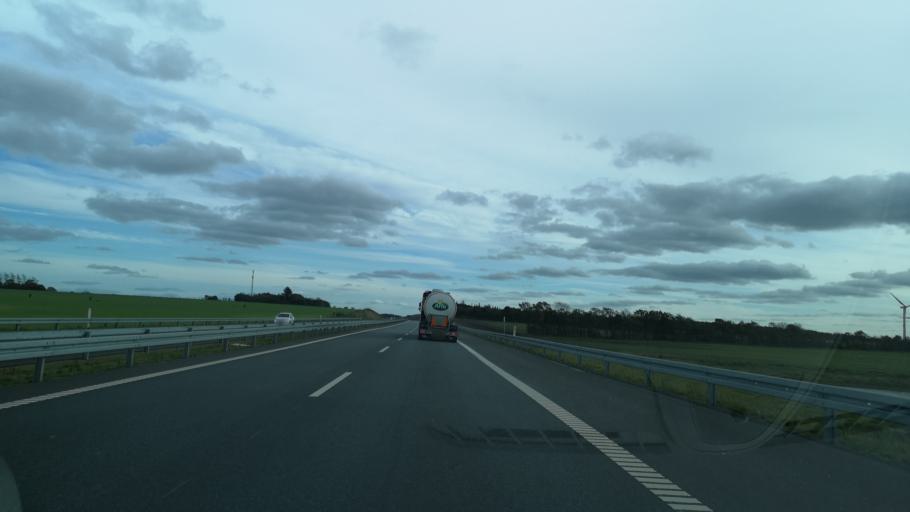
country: DK
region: Central Jutland
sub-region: Herning Kommune
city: Avlum
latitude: 56.2740
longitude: 8.7473
